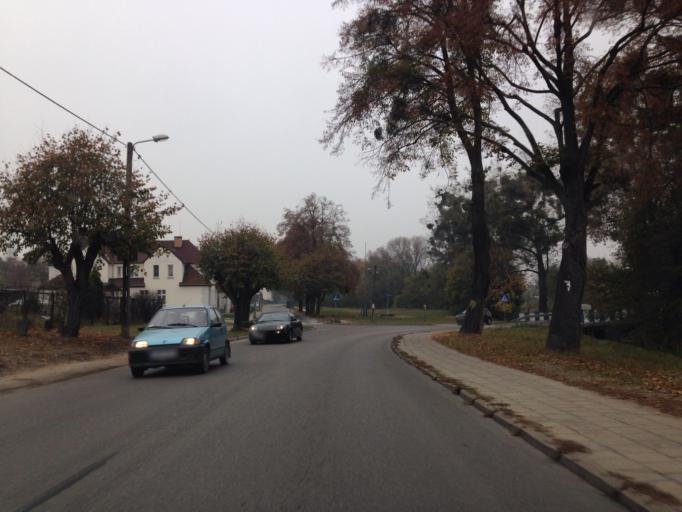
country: PL
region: Kujawsko-Pomorskie
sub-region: Powiat brodnicki
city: Brodnica
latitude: 53.2657
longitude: 19.3913
